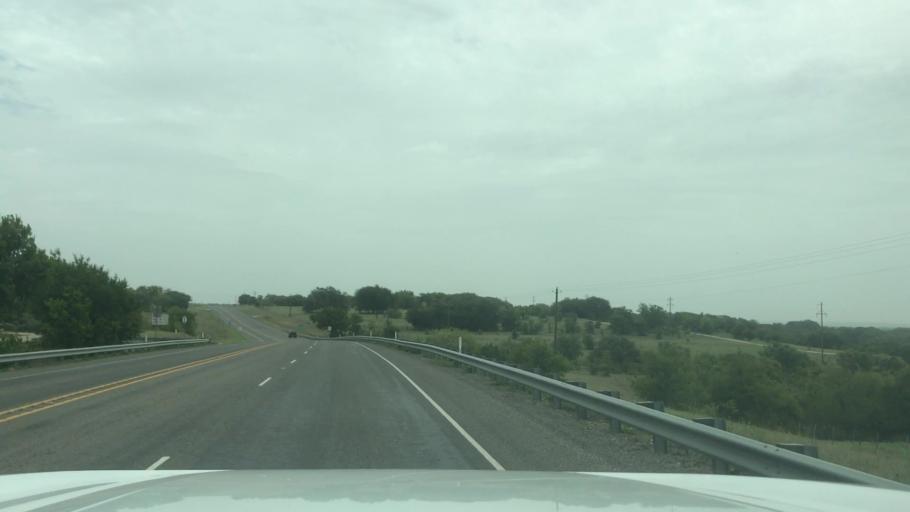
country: US
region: Texas
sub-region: Hamilton County
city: Hico
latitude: 31.9808
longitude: -98.0225
